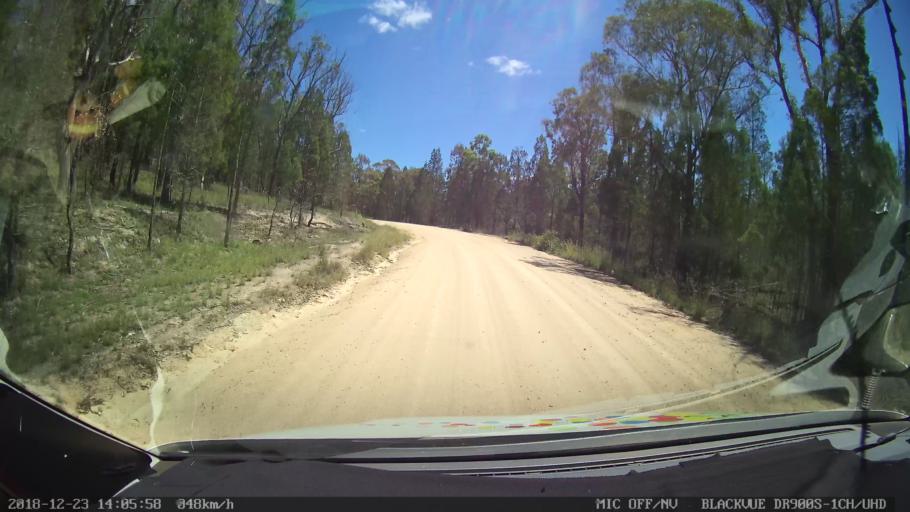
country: AU
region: New South Wales
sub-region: Tamworth Municipality
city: Manilla
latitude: -30.6274
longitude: 151.0774
